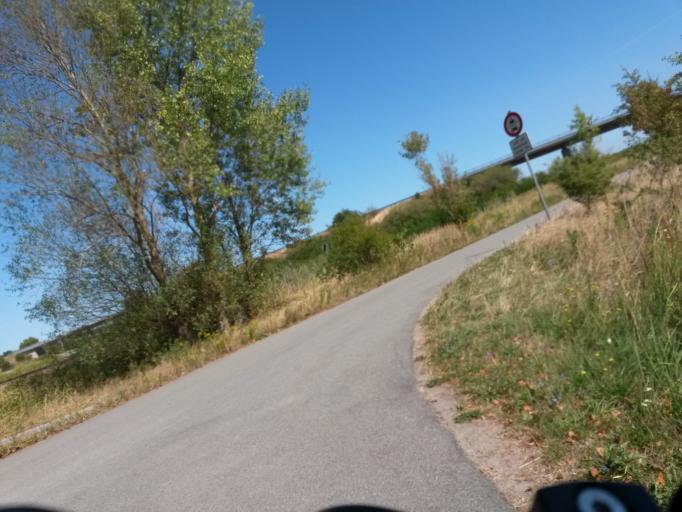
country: DE
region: Saxony-Anhalt
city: Hassel
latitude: 52.5974
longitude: 11.9577
